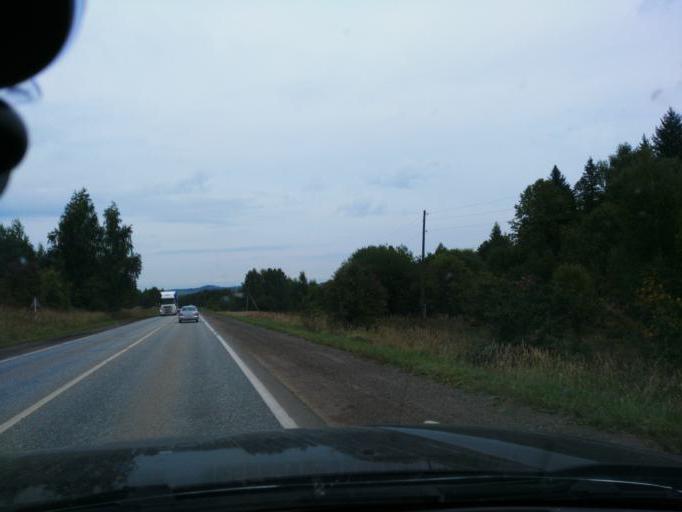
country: RU
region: Perm
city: Chernushka
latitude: 56.5877
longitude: 56.1498
